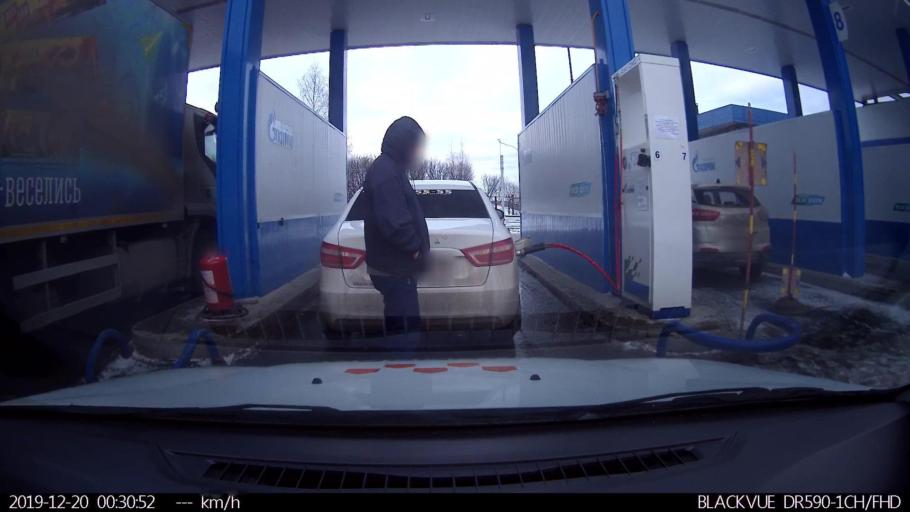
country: RU
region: Vladimir
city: Yur'yev-Pol'skiy
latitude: 56.5168
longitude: 39.6492
